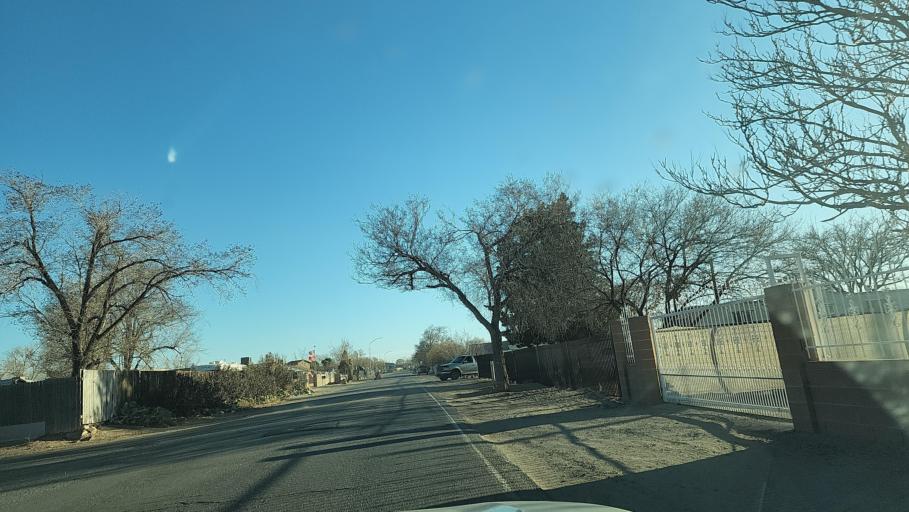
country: US
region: New Mexico
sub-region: Bernalillo County
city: South Valley
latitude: 35.0187
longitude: -106.6549
